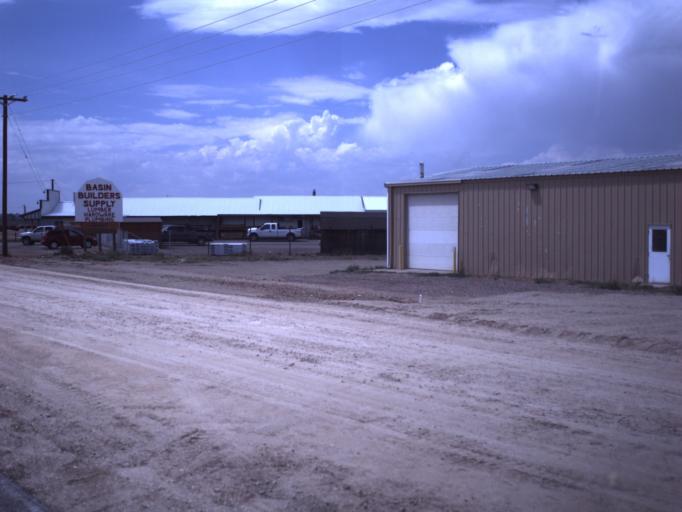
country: US
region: Utah
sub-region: Duchesne County
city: Roosevelt
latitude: 40.2704
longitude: -110.0360
